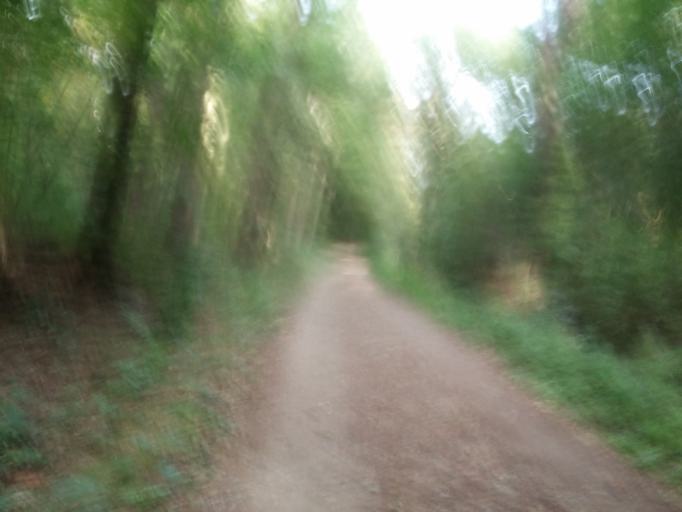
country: DE
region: North Rhine-Westphalia
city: Dorsten
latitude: 51.6519
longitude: 7.0063
